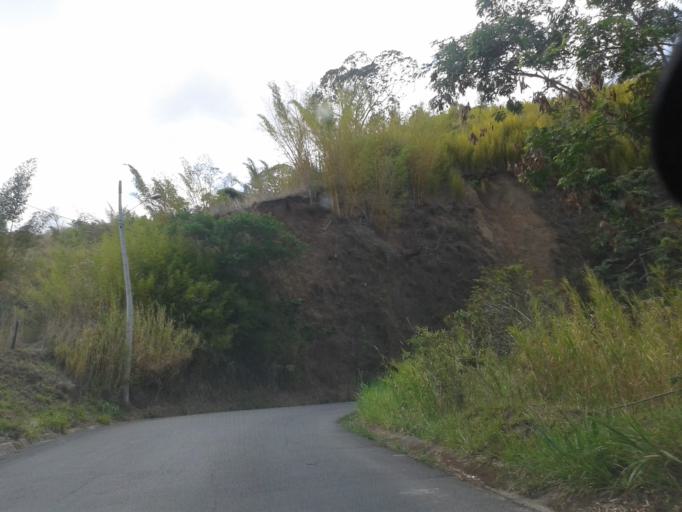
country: CR
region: Alajuela
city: Sabanilla
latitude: 10.0523
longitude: -84.2057
